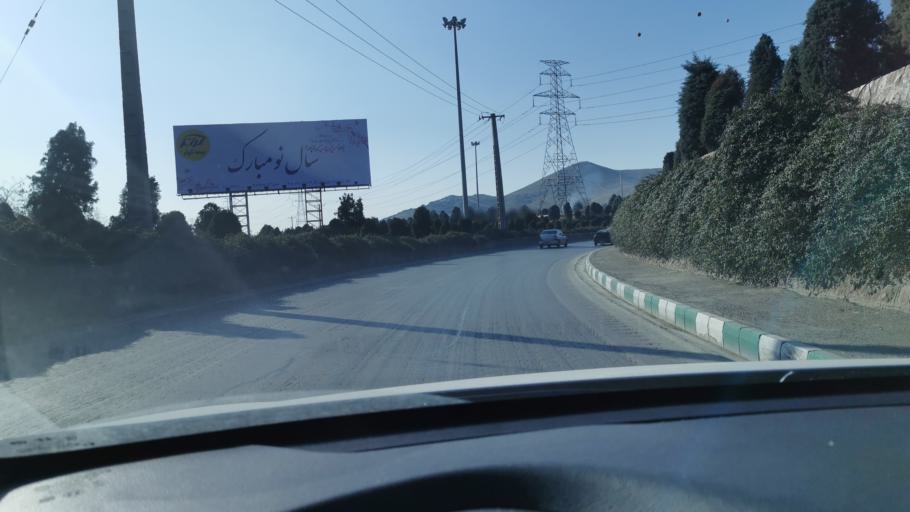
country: IR
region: Razavi Khorasan
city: Mashhad
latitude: 36.2650
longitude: 59.5809
